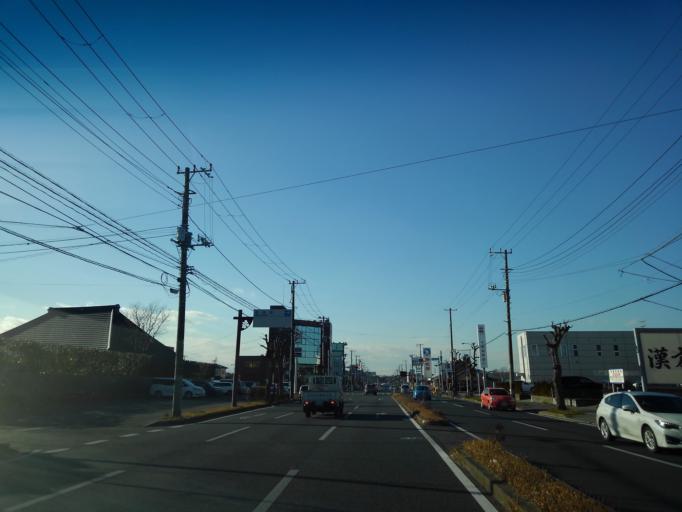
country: JP
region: Chiba
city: Kimitsu
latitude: 35.3304
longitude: 139.8941
